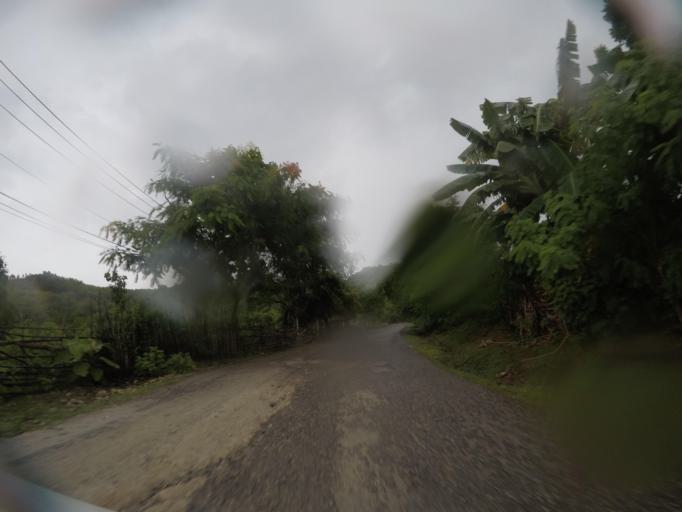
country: ID
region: East Nusa Tenggara
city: Atambua
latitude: -8.9674
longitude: 125.0250
